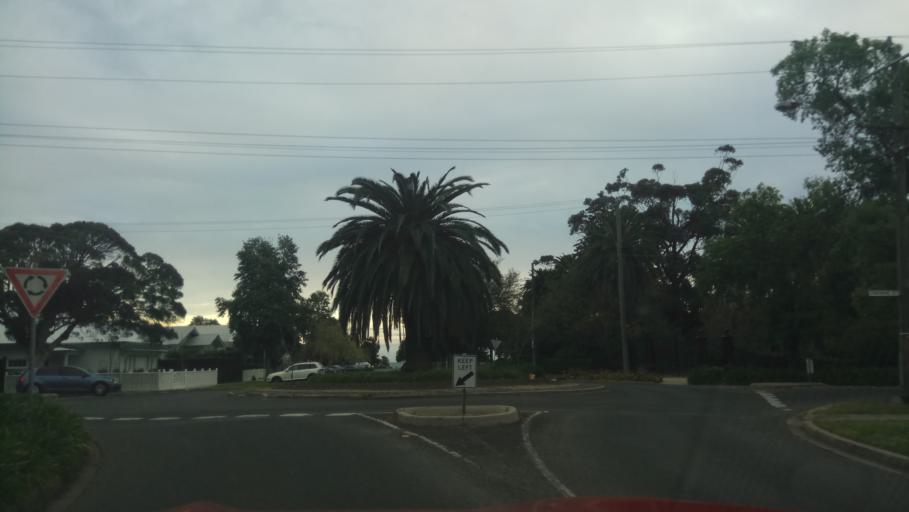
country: AU
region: Victoria
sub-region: Hobsons Bay
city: Williamstown
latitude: -37.8665
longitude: 144.8986
